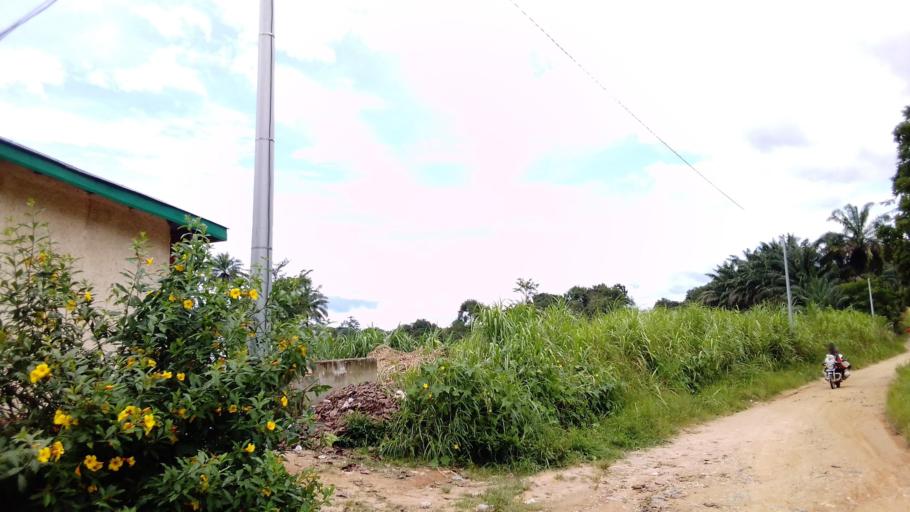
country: SL
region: Eastern Province
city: Koyima
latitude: 8.6975
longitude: -11.0102
